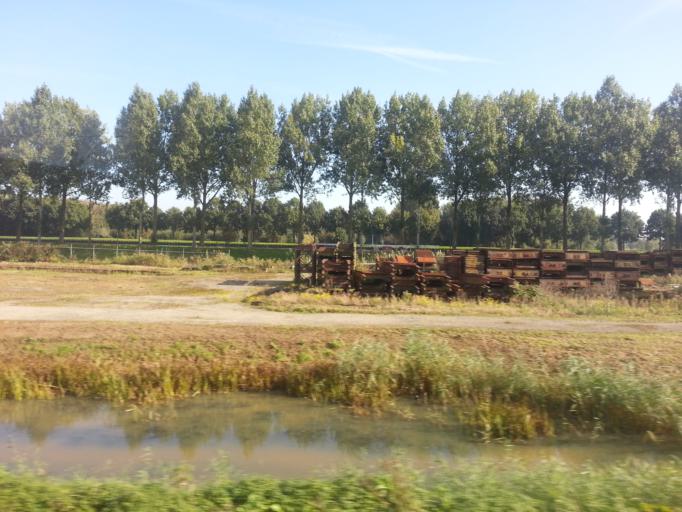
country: NL
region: Utrecht
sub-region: Stichtse Vecht
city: Breukelen
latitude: 52.1569
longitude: 4.9979
